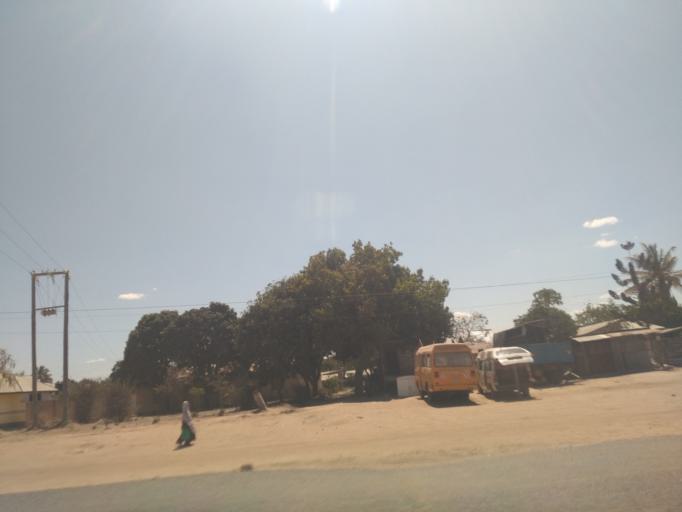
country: TZ
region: Dodoma
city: Dodoma
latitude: -6.1585
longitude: 35.7466
